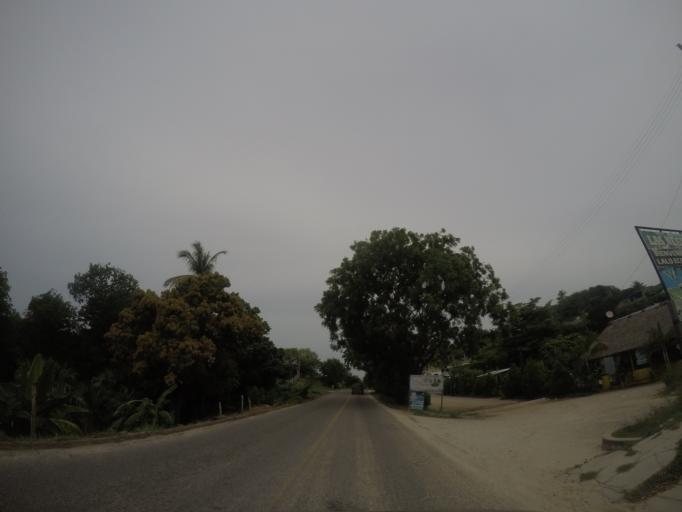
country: MX
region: Oaxaca
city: San Pedro Mixtepec
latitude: 15.9465
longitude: -97.1853
